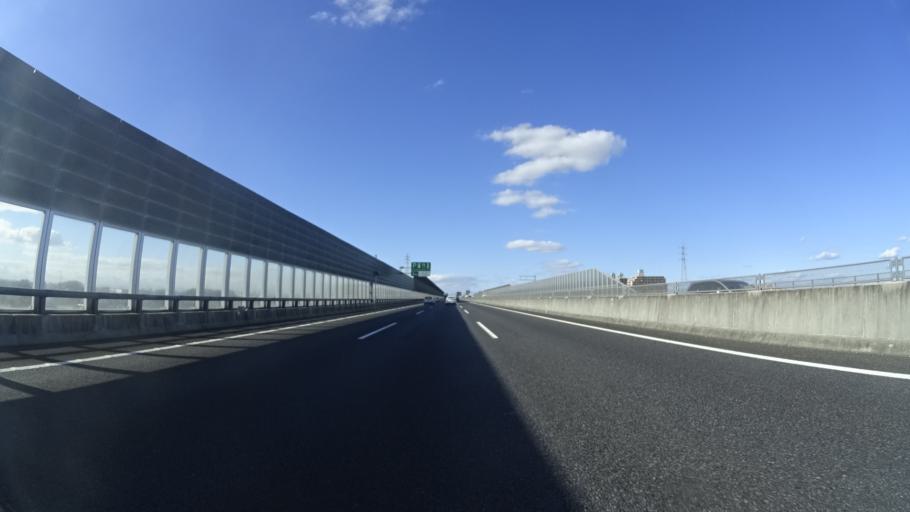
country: JP
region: Aichi
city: Chiryu
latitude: 35.0312
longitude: 137.0586
